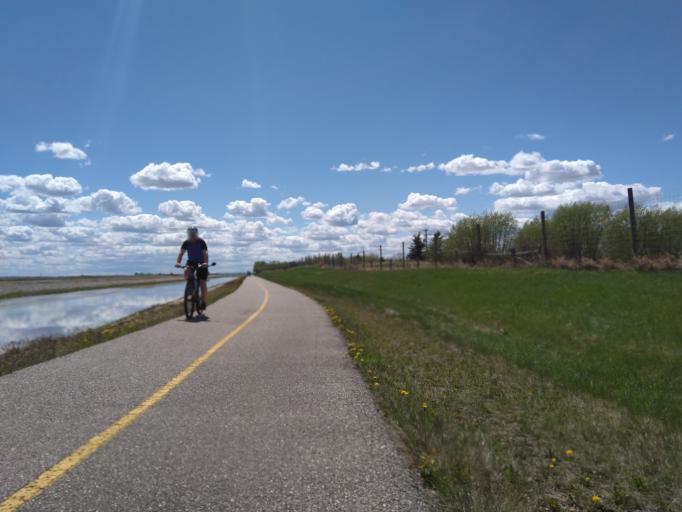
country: CA
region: Alberta
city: Chestermere
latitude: 51.0005
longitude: -113.8591
